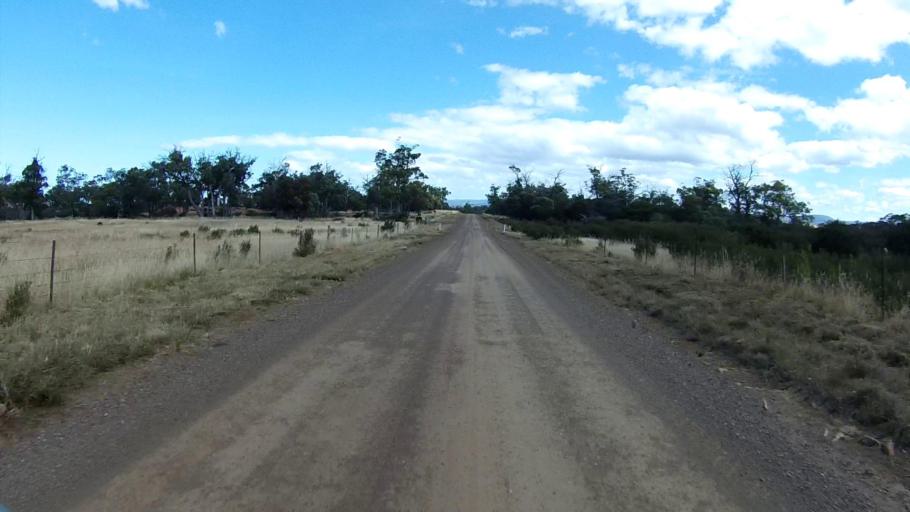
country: AU
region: Tasmania
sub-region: Break O'Day
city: St Helens
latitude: -41.9789
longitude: 148.0684
